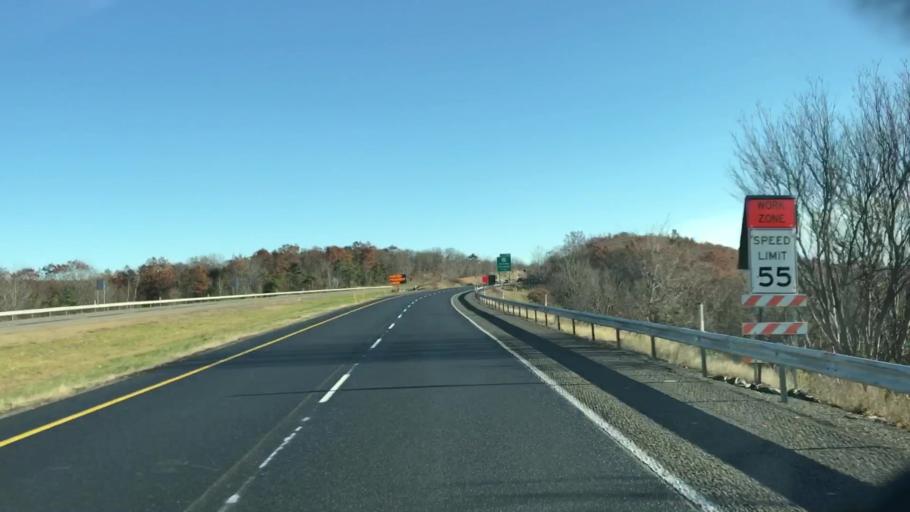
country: US
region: Pennsylvania
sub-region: Schuylkill County
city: McAdoo
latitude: 40.8698
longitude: -76.0334
